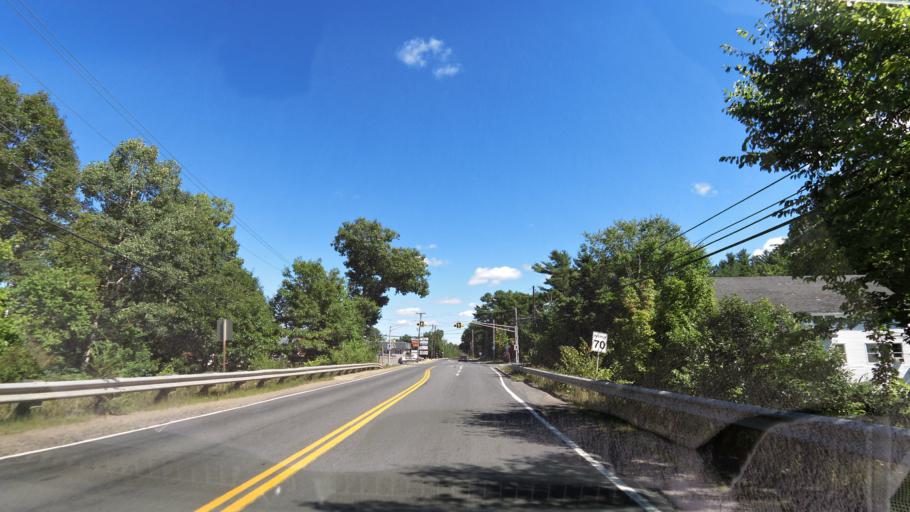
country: CA
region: Nova Scotia
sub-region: Kings County
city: Kentville
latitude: 45.0611
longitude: -64.6013
